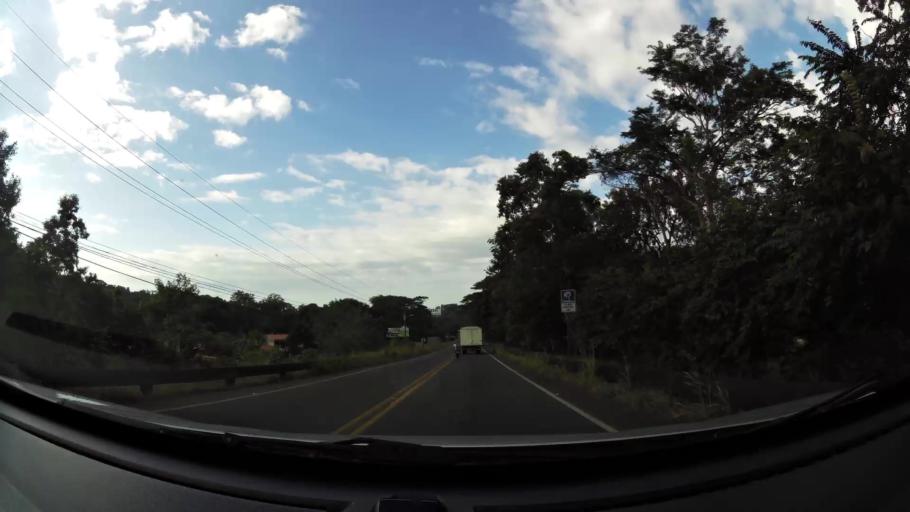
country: CR
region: Puntarenas
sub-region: Canton de Garabito
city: Jaco
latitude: 9.7071
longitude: -84.6350
